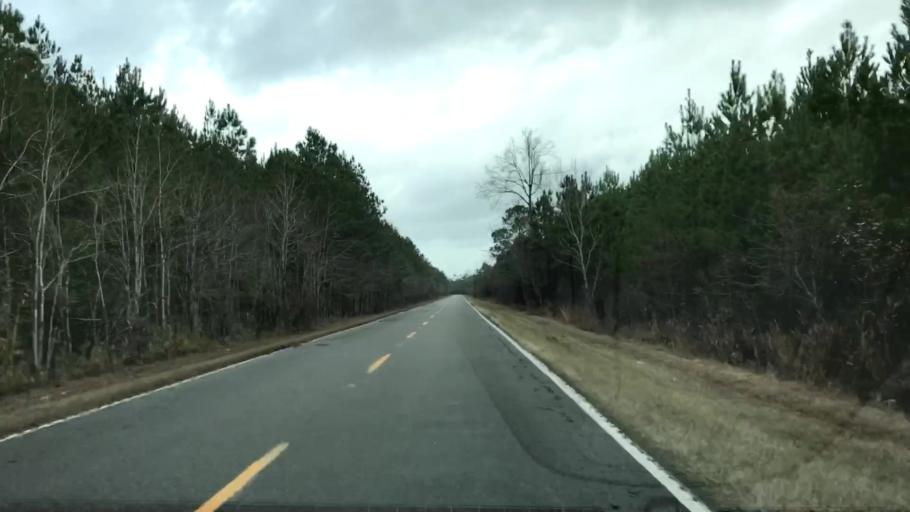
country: US
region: South Carolina
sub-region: Georgetown County
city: Murrells Inlet
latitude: 33.6274
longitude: -79.2431
